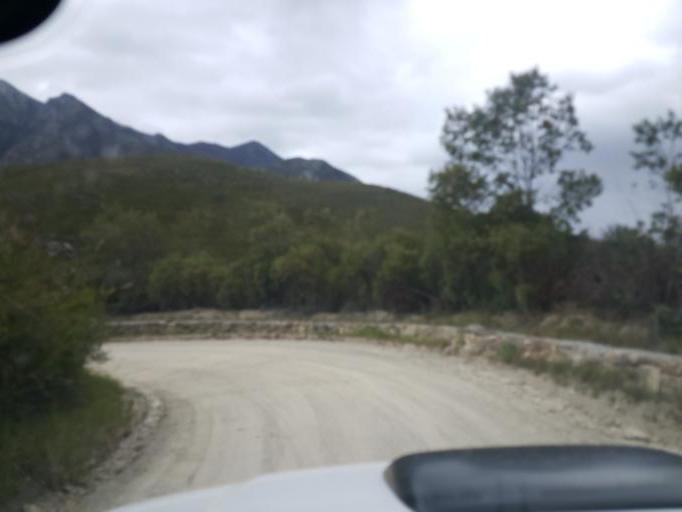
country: ZA
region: Western Cape
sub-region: Eden District Municipality
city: George
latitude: -33.9133
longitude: 22.4158
